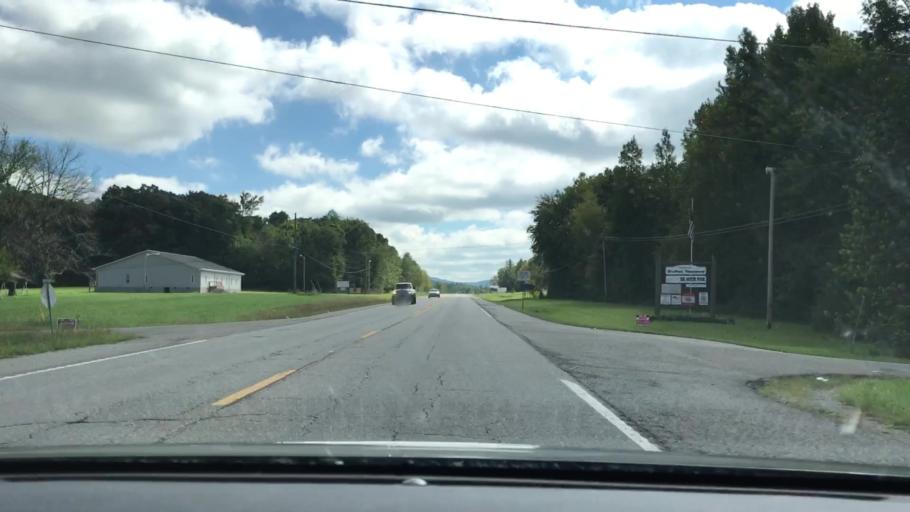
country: US
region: Kentucky
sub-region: McCreary County
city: Pine Knot
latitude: 36.5906
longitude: -84.4391
